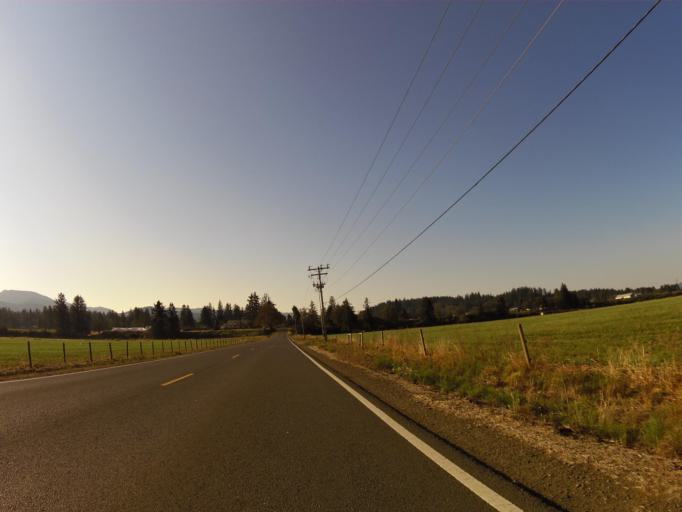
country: US
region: Oregon
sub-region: Tillamook County
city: Tillamook
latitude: 45.4348
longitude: -123.7780
